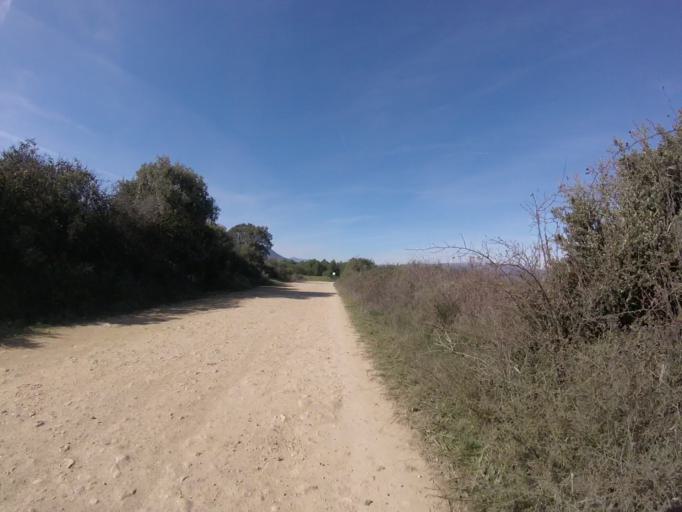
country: ES
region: Navarre
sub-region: Provincia de Navarra
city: Oteiza
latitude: 42.6423
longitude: -1.9558
